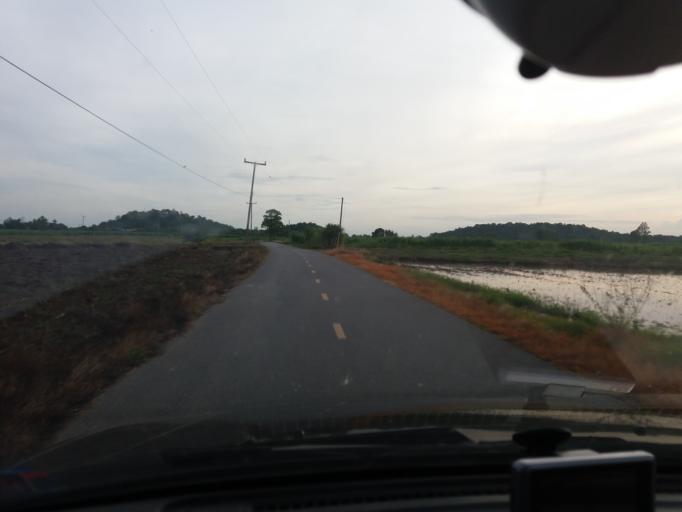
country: TH
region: Suphan Buri
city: Doembang Nangbuat
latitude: 14.8236
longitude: 100.1408
